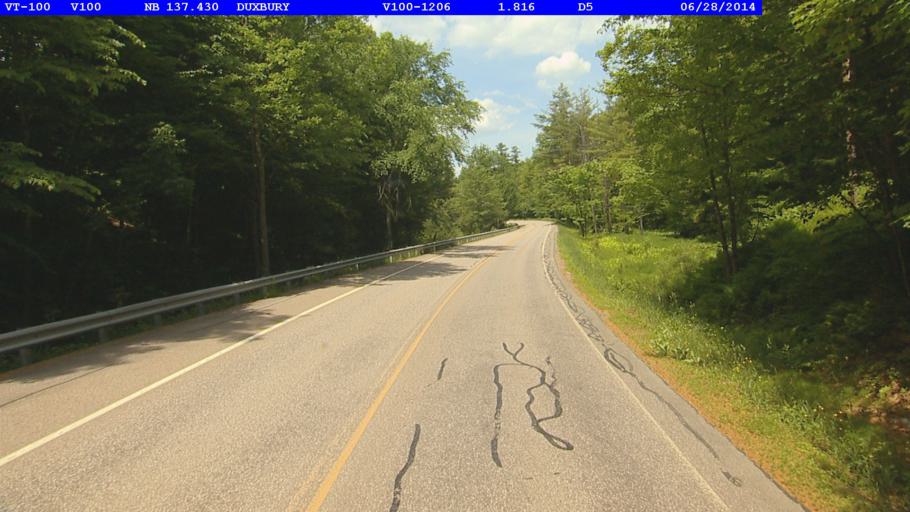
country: US
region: Vermont
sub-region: Washington County
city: Waterbury
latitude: 44.2720
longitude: -72.7855
